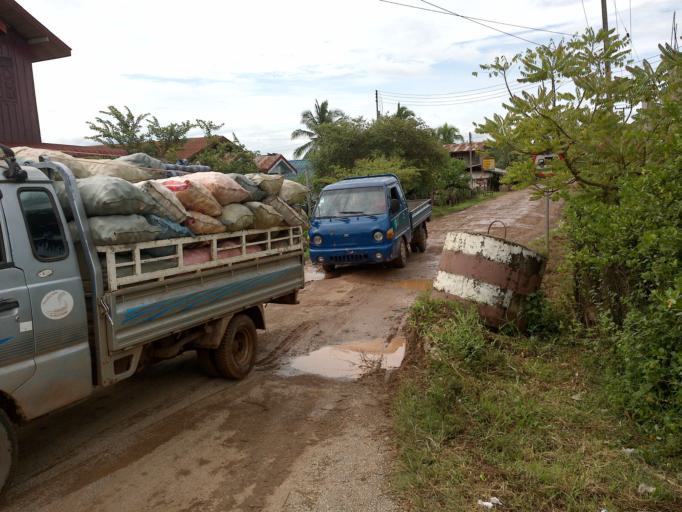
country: LA
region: Xiagnabouli
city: Sainyabuli
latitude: 19.1832
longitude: 101.6361
